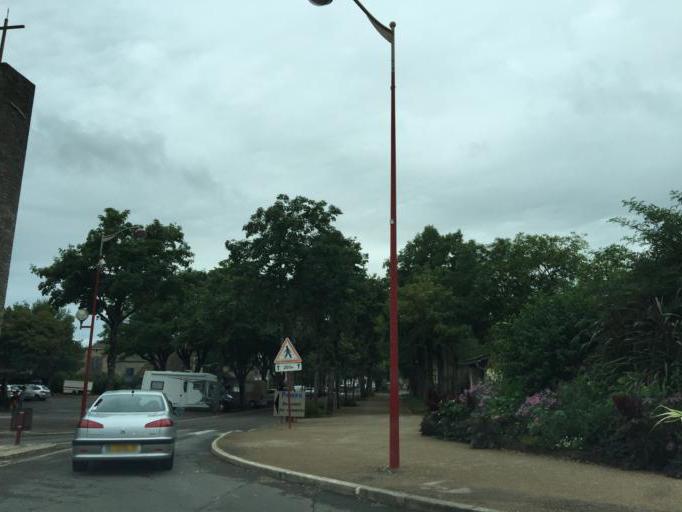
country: FR
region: Midi-Pyrenees
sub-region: Departement de l'Aveyron
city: Bozouls
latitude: 44.4714
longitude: 2.7227
